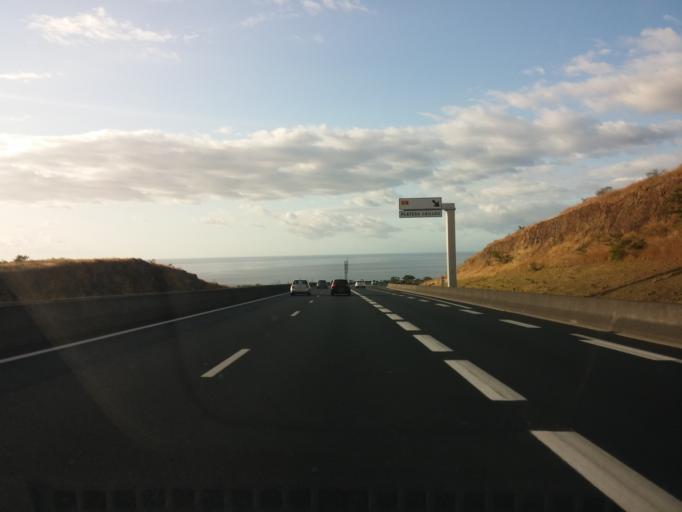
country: RE
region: Reunion
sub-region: Reunion
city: Saint-Paul
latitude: -21.0249
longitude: 55.2561
